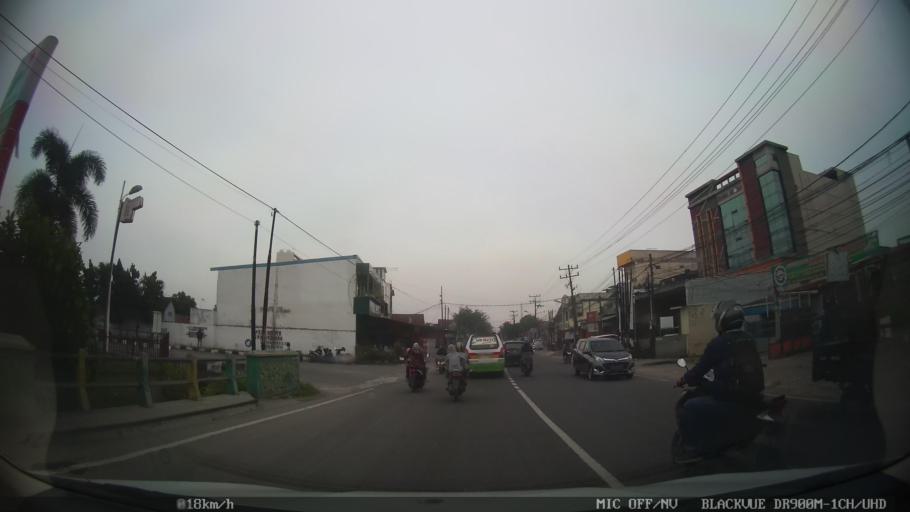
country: ID
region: North Sumatra
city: Deli Tua
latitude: 3.5410
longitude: 98.7172
